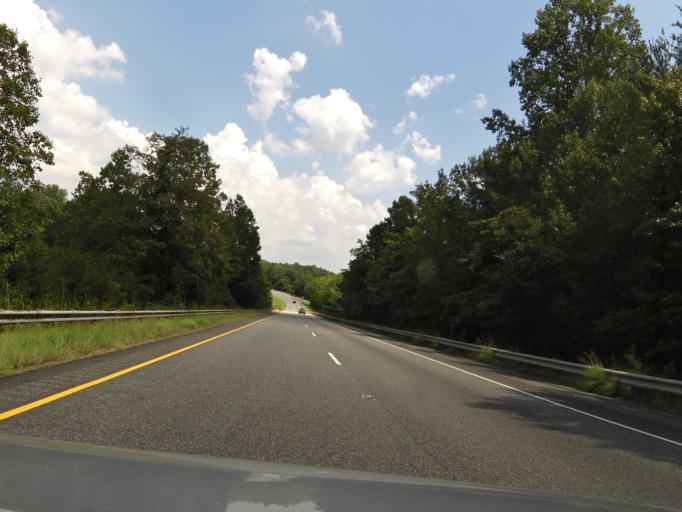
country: US
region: North Carolina
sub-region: Polk County
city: Columbus
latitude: 35.2509
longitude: -82.2094
